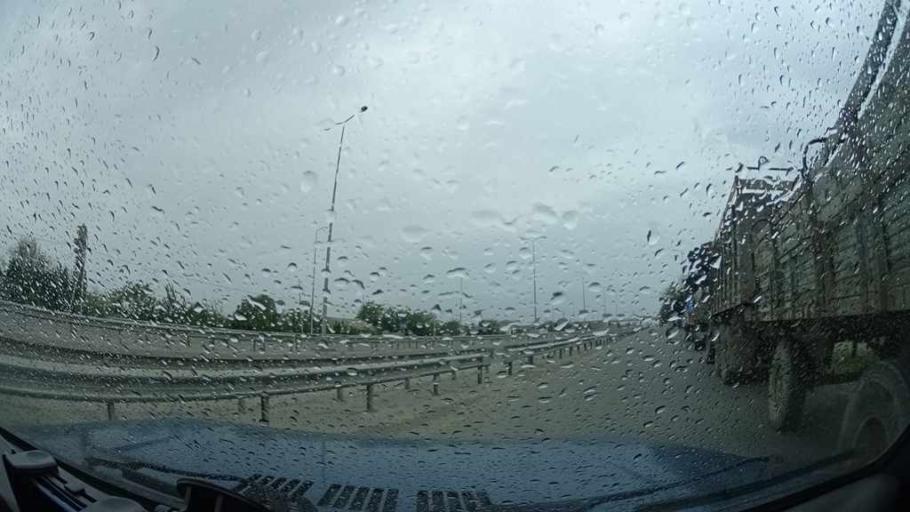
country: AZ
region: Samux
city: Samux
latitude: 40.6892
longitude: 46.5558
